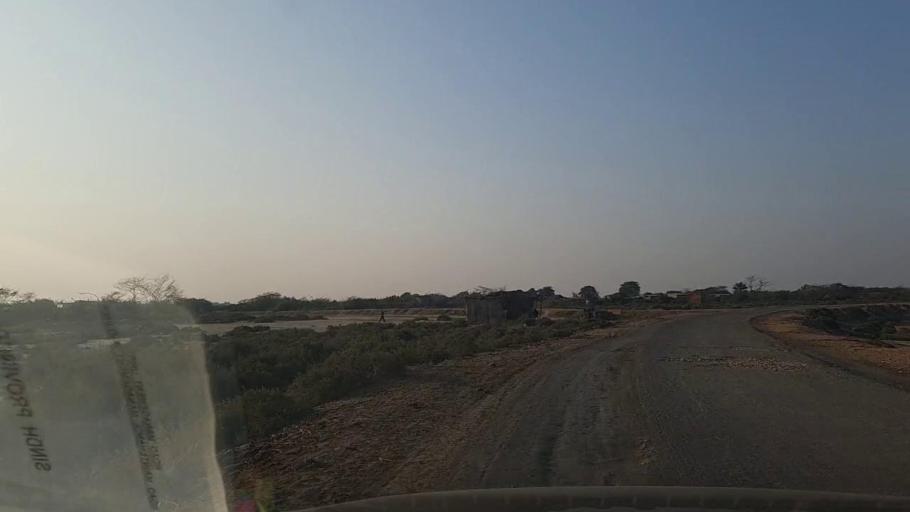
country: PK
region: Sindh
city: Keti Bandar
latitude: 24.2892
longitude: 67.5835
